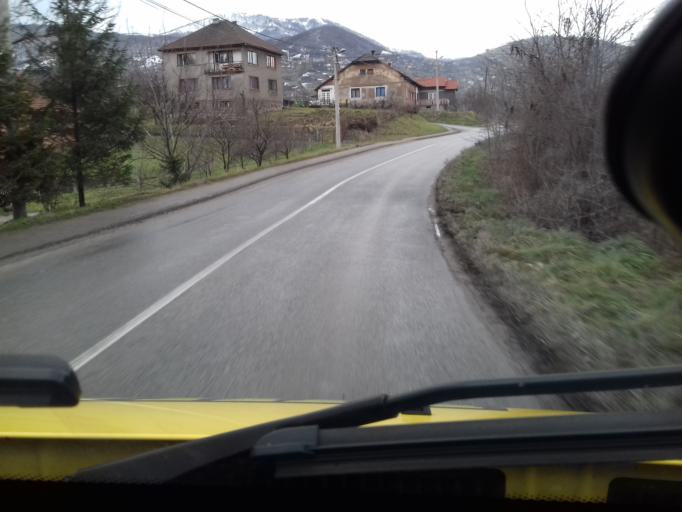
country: BA
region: Federation of Bosnia and Herzegovina
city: Zenica
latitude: 44.2267
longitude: 17.8906
